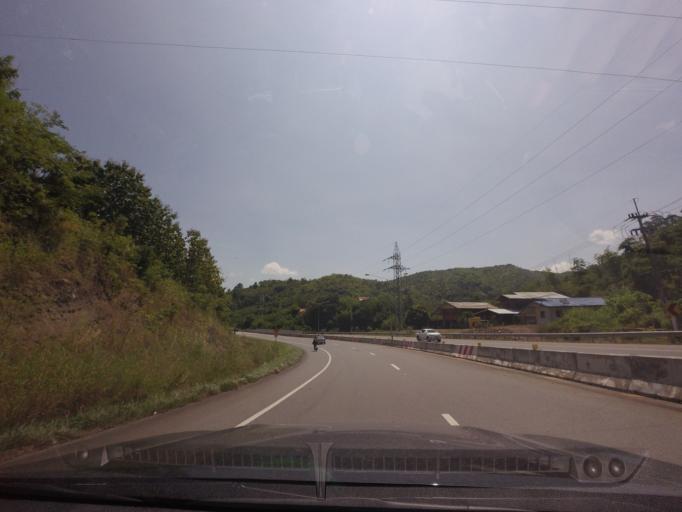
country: TH
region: Phetchabun
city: Lom Sak
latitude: 16.7641
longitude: 101.1409
